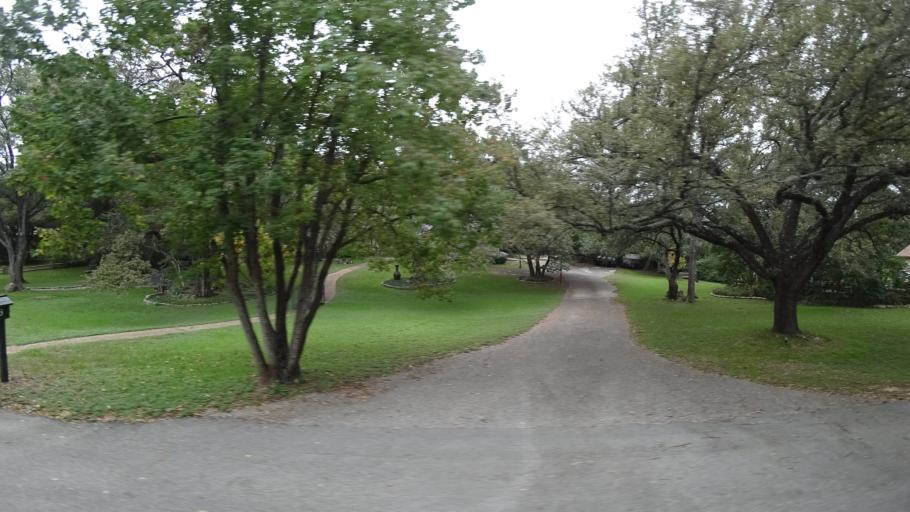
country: US
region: Texas
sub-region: Williamson County
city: Anderson Mill
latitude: 30.4492
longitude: -97.8232
